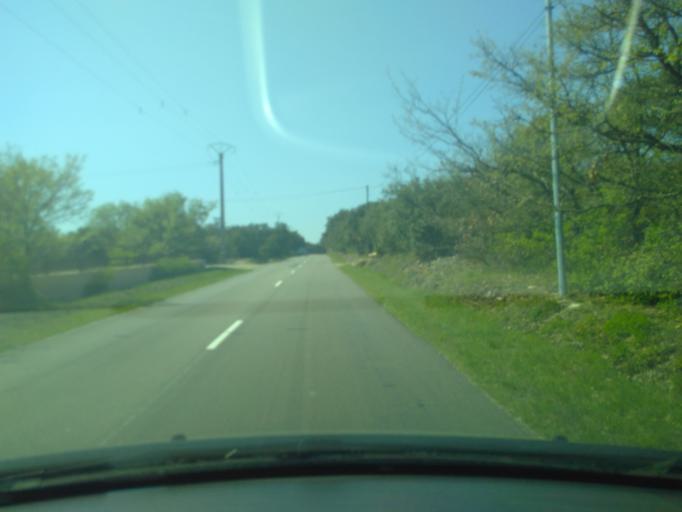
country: FR
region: Rhone-Alpes
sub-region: Departement de la Drome
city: Taulignan
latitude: 44.4459
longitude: 4.9584
